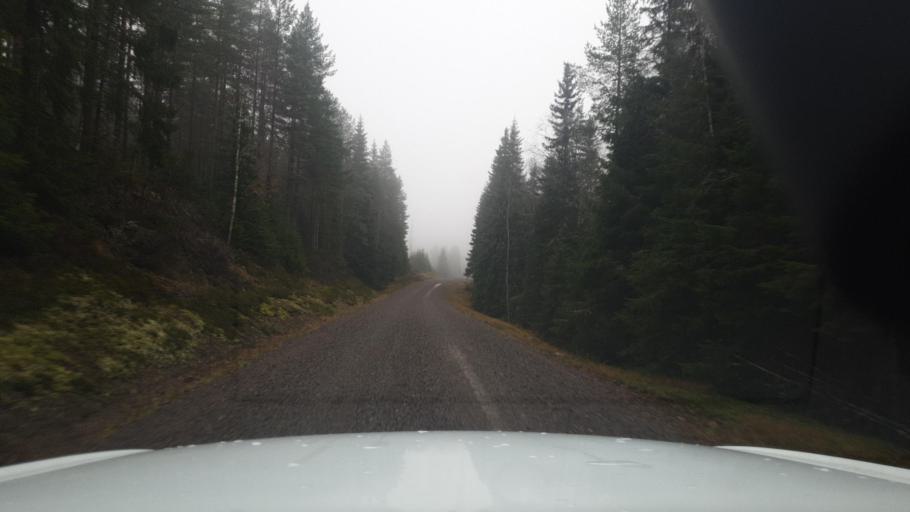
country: SE
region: Vaermland
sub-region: Eda Kommun
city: Charlottenberg
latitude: 60.0939
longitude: 12.6133
